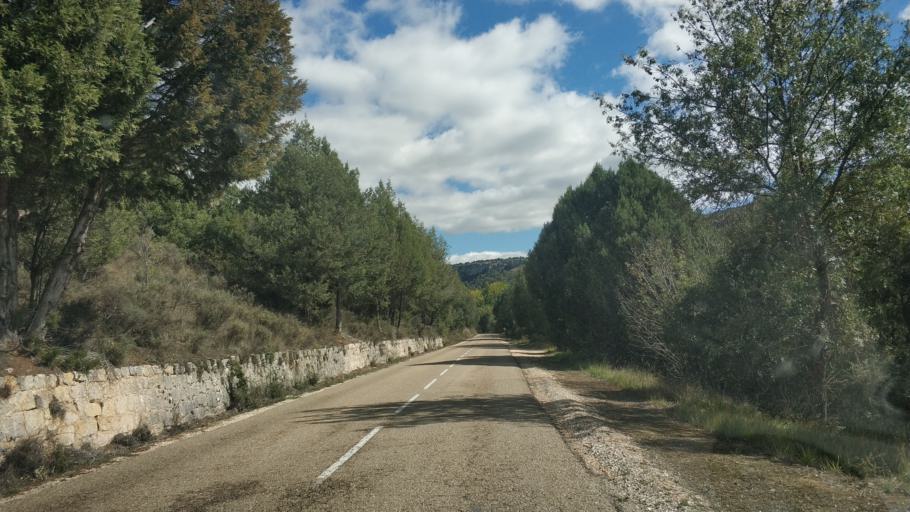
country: ES
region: Castille and Leon
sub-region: Provincia de Burgos
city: Hortiguela
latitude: 42.0485
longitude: -3.4648
